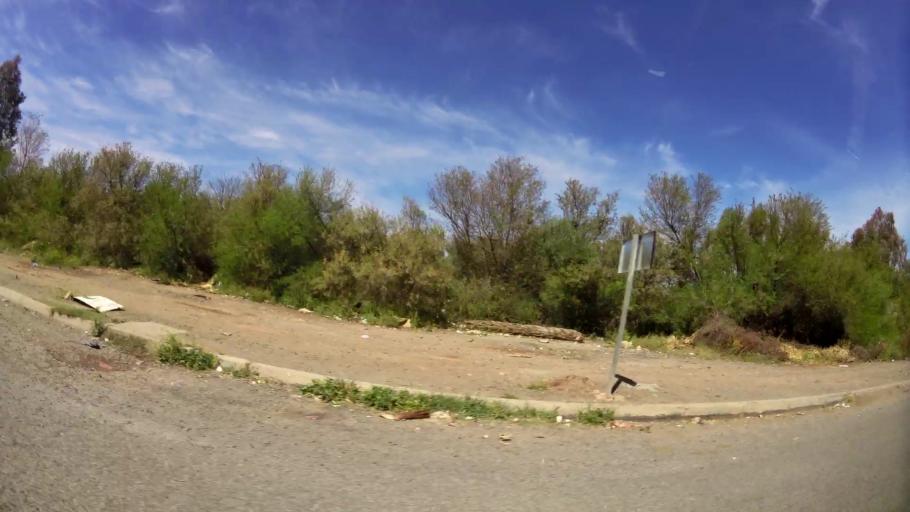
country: MA
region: Marrakech-Tensift-Al Haouz
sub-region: Marrakech
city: Marrakesh
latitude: 31.6425
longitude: -8.1081
